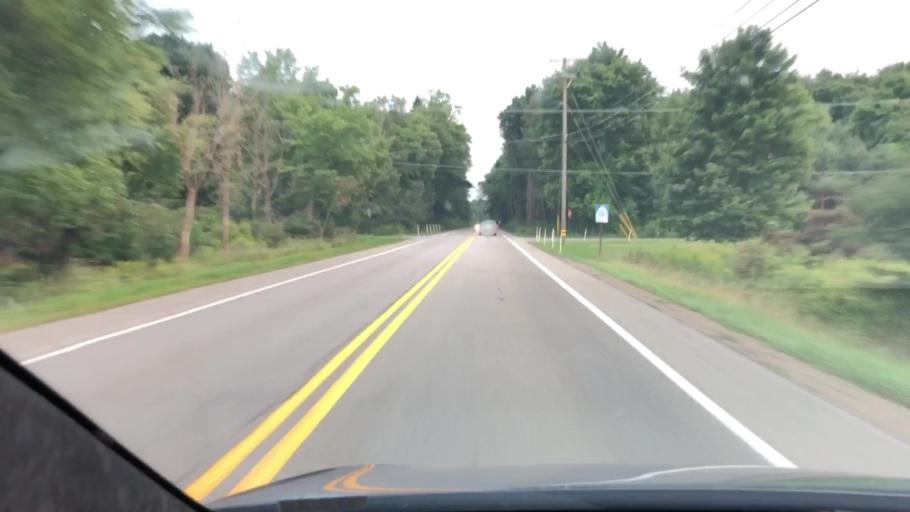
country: US
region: Pennsylvania
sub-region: Butler County
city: Slippery Rock
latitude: 41.0174
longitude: -80.0056
